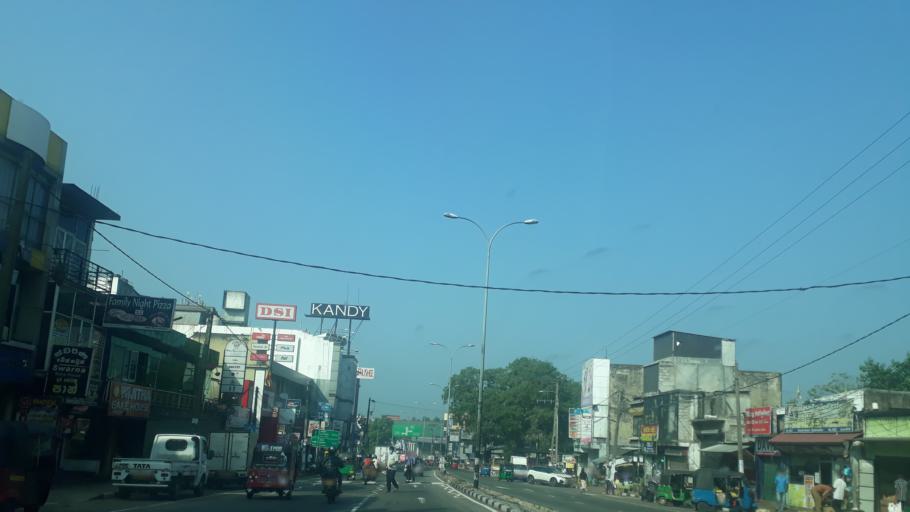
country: LK
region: Western
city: Kelaniya
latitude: 7.0023
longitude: 79.9524
